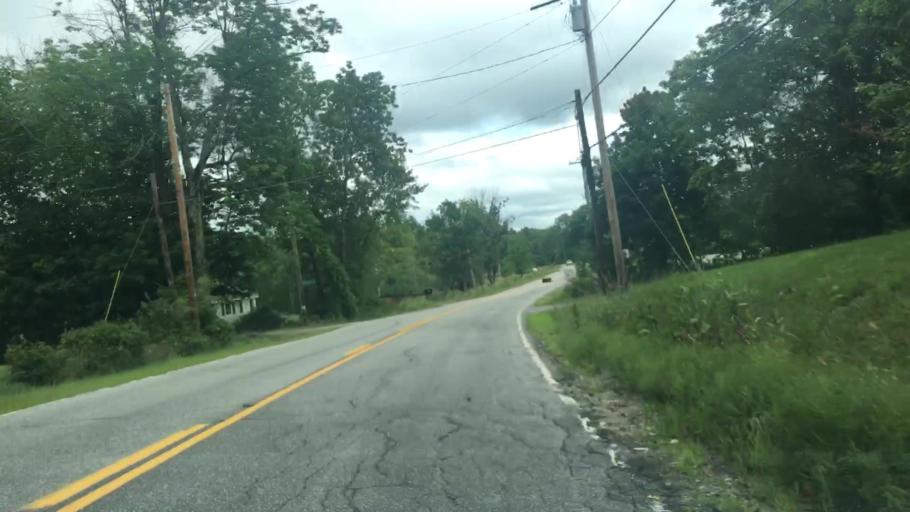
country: US
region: Maine
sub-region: York County
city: Limerick
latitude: 43.6765
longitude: -70.7839
